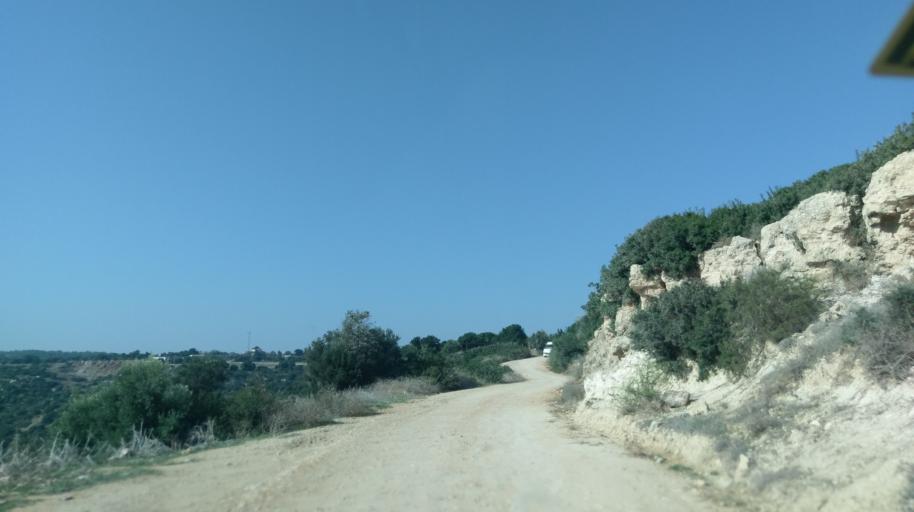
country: CY
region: Ammochostos
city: Leonarisso
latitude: 35.4863
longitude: 34.2196
